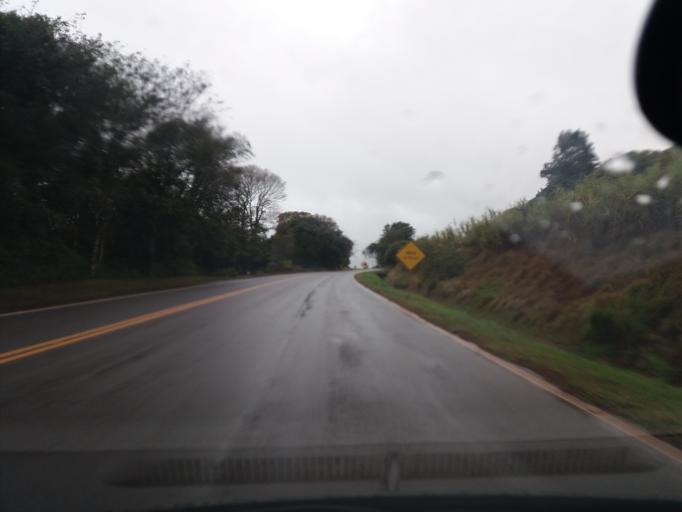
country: BR
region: Parana
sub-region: Campo Mourao
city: Campo Mourao
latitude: -24.3198
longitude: -52.6389
